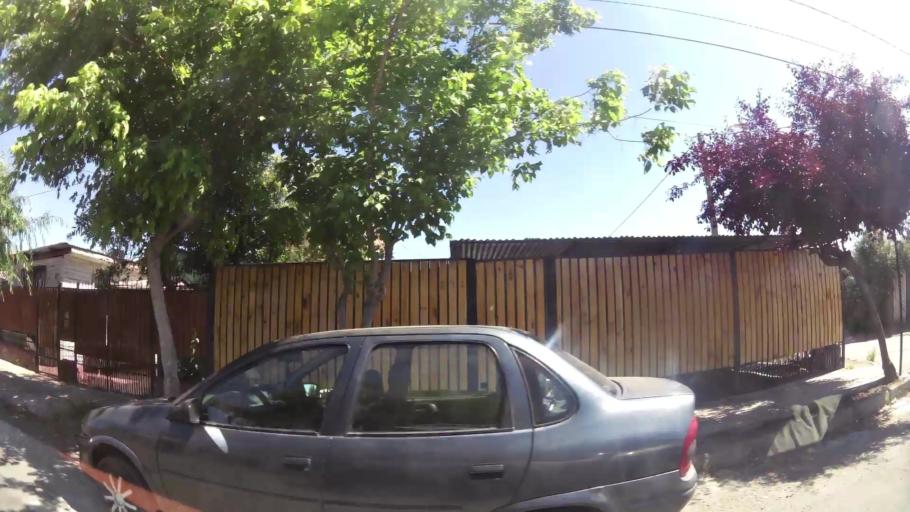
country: CL
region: Santiago Metropolitan
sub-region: Provincia de Maipo
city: San Bernardo
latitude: -33.5761
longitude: -70.6777
